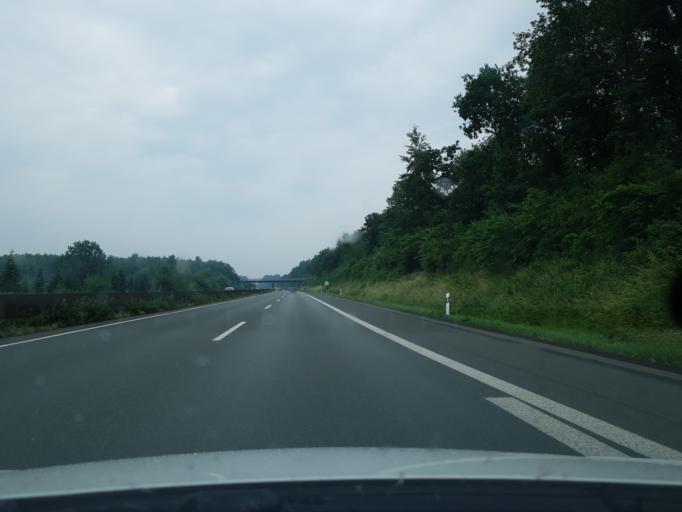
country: DE
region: North Rhine-Westphalia
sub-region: Regierungsbezirk Munster
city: Velen
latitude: 51.8942
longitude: 7.0222
